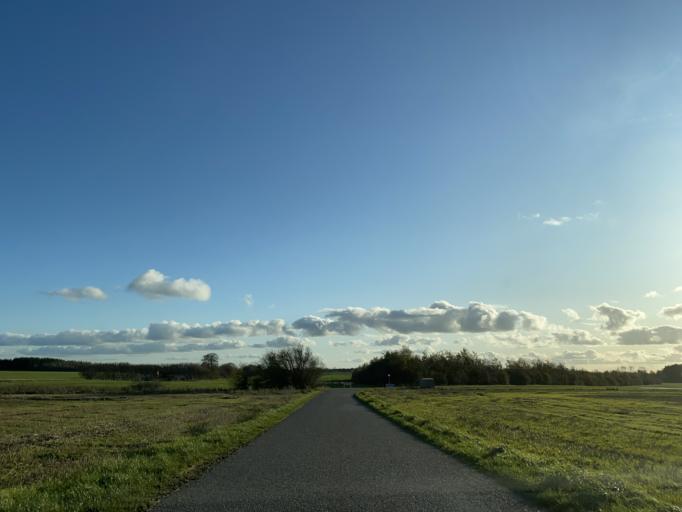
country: DK
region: Central Jutland
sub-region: Viborg Kommune
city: Bjerringbro
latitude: 56.3288
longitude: 9.7090
